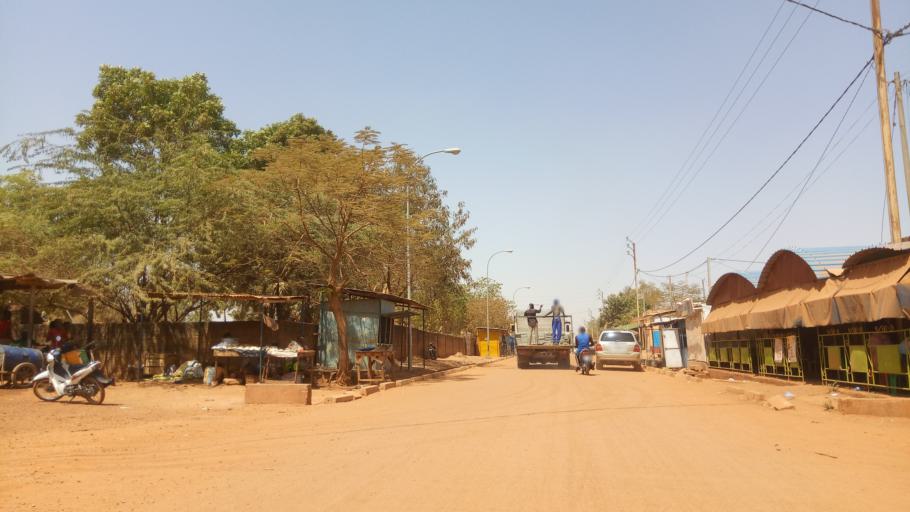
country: BF
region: Centre
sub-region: Kadiogo Province
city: Ouagadougou
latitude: 12.3930
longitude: -1.5636
